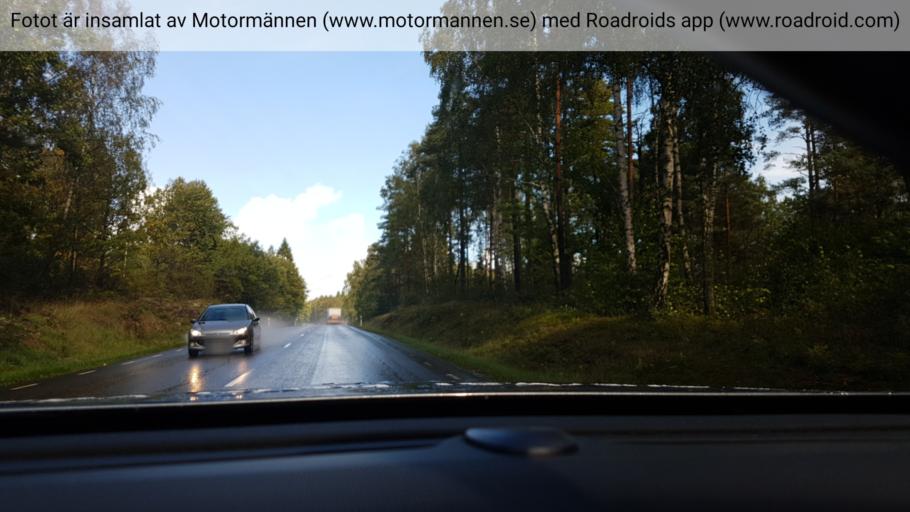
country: SE
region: Vaestra Goetaland
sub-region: Alingsas Kommun
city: Alingsas
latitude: 58.0108
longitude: 12.4475
